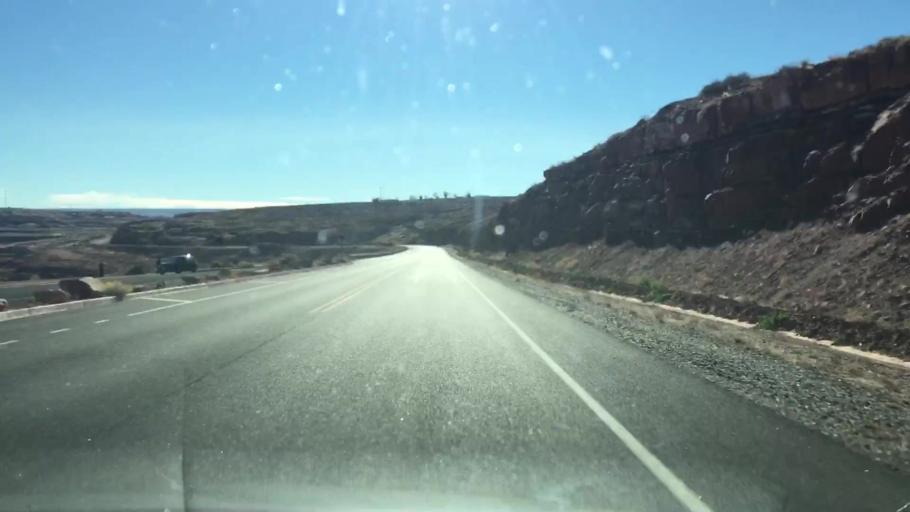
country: US
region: Arizona
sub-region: Coconino County
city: Page
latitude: 36.9647
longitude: -111.4913
